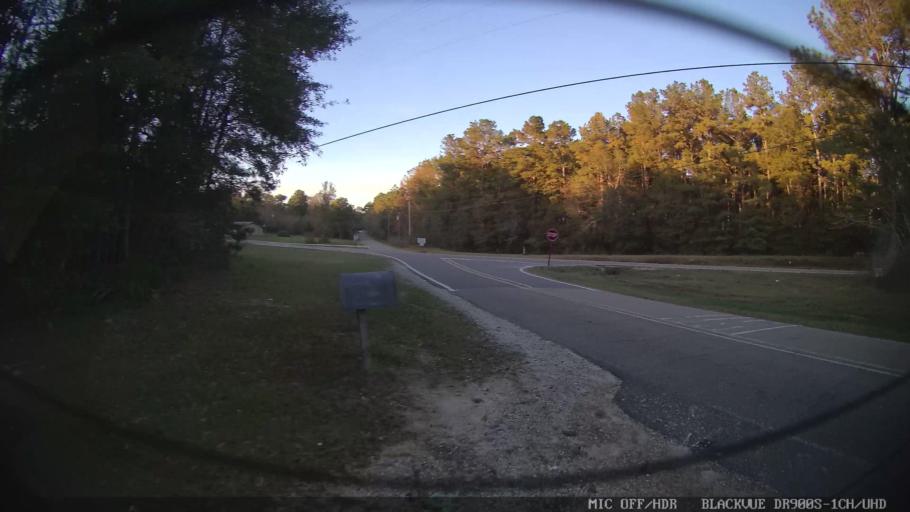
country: US
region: Mississippi
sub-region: Stone County
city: Wiggins
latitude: 30.9865
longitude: -89.2587
